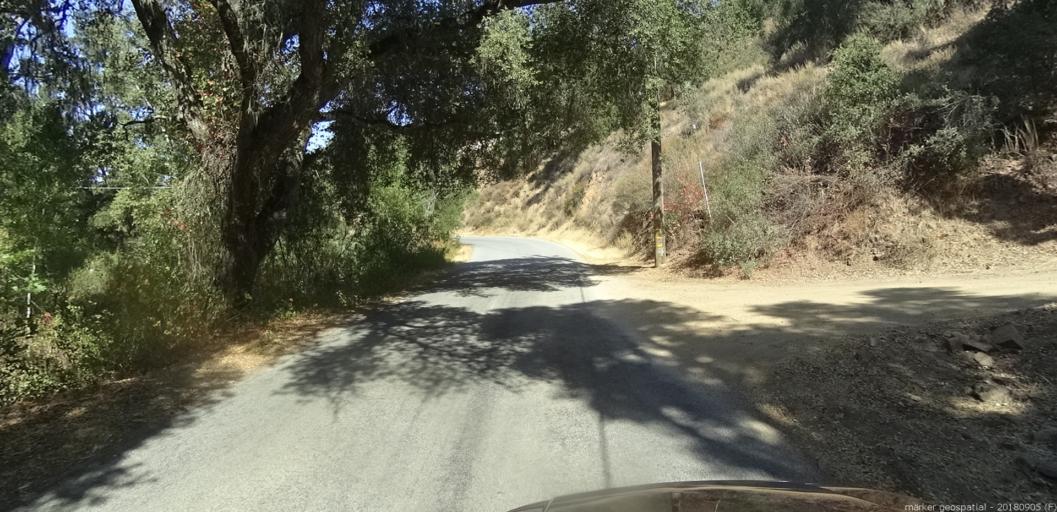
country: US
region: California
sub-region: Monterey County
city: Carmel Valley Village
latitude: 36.3915
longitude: -121.6294
